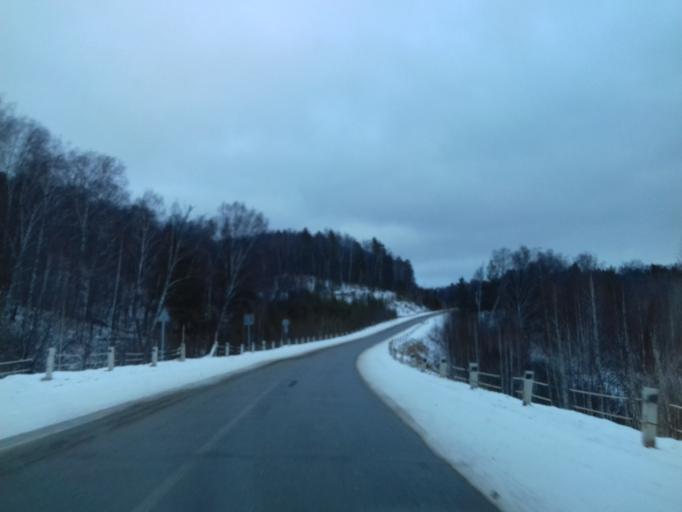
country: RU
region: Bashkortostan
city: Starosubkhangulovo
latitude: 53.2309
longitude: 57.4610
